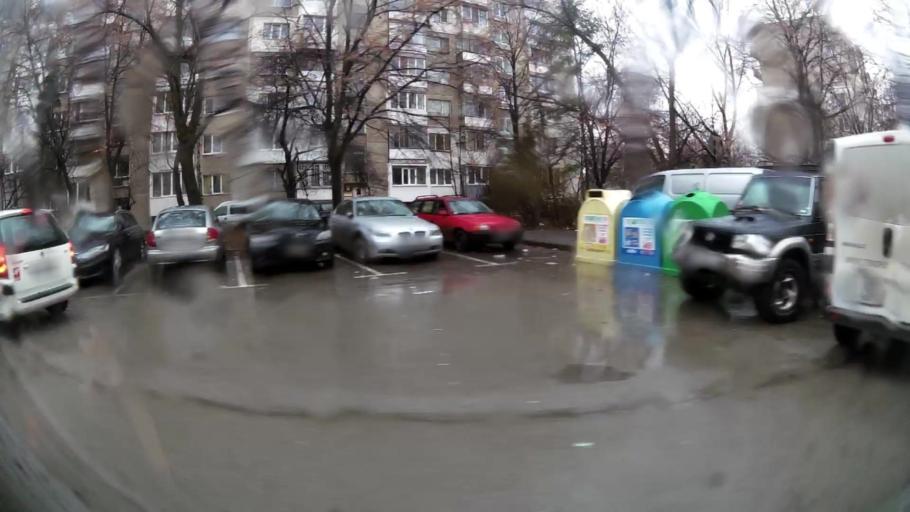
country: BG
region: Sofia-Capital
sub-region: Stolichna Obshtina
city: Sofia
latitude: 42.6541
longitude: 23.3764
